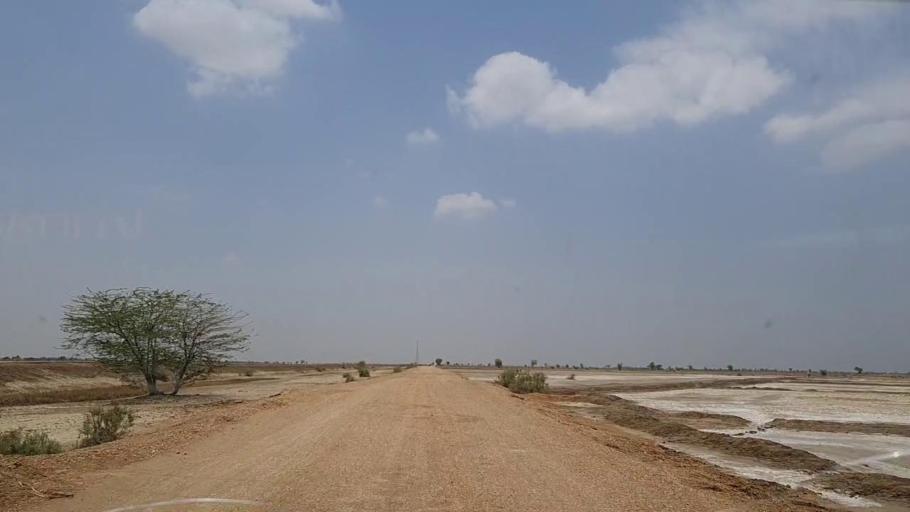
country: PK
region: Sindh
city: Johi
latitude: 26.7712
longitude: 67.6568
